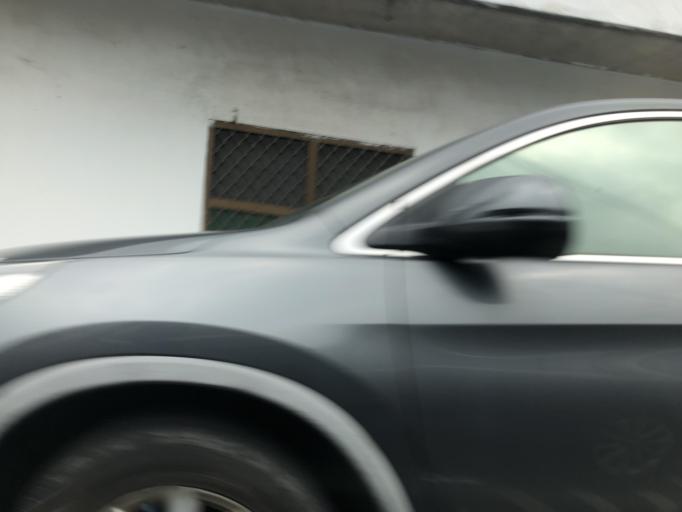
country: TW
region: Taiwan
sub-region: Keelung
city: Keelung
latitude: 25.2173
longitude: 121.6481
